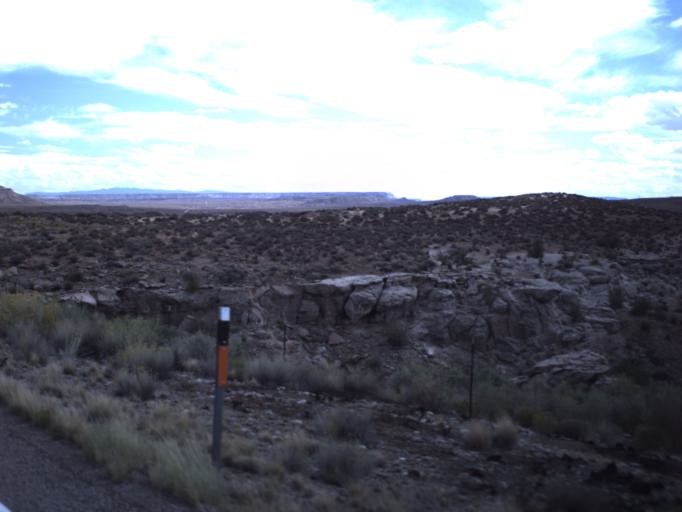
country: US
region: Utah
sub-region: San Juan County
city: Blanding
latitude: 37.2782
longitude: -109.3620
